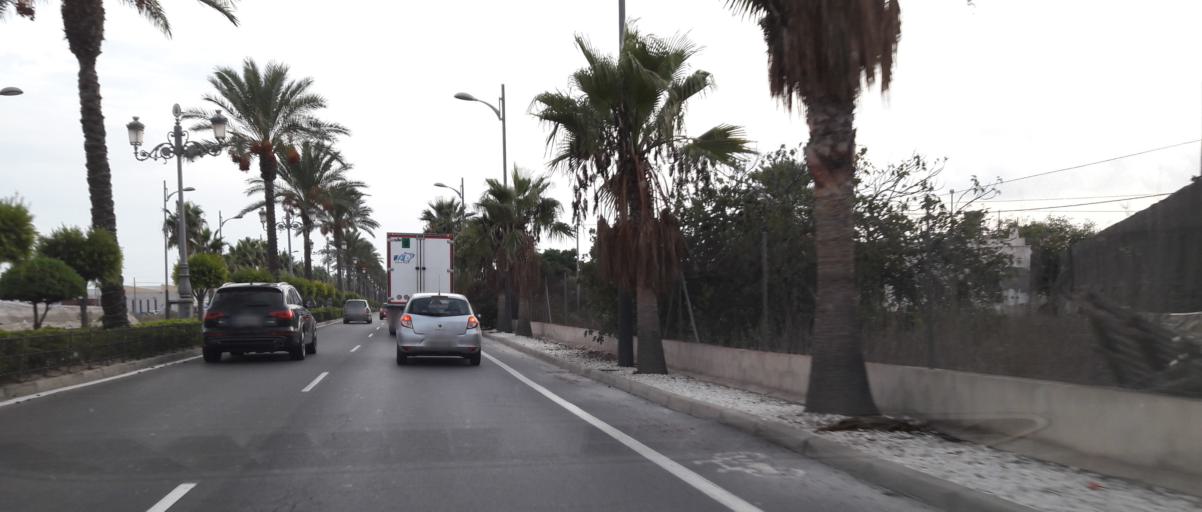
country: ES
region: Andalusia
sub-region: Provincia de Almeria
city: Roquetas de Mar
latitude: 36.7913
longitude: -2.6048
